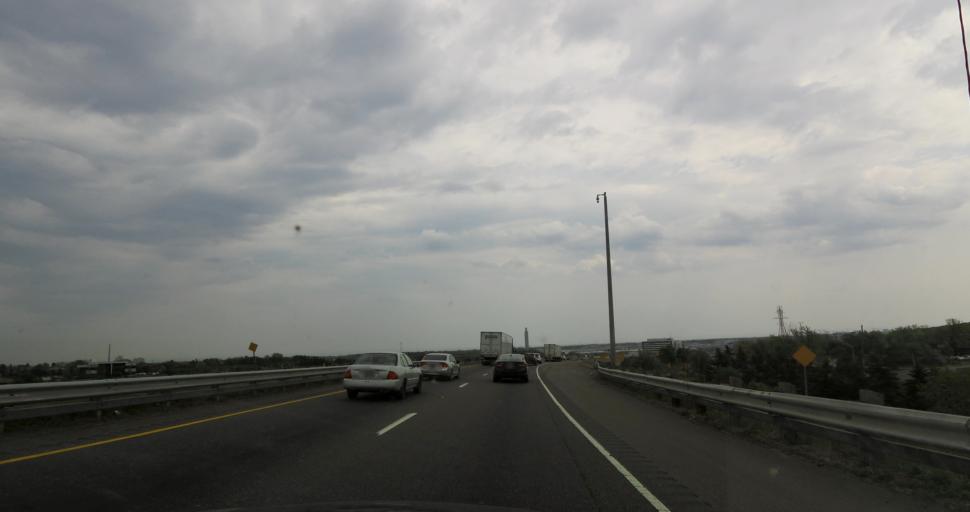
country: CA
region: Ontario
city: Oakville
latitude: 43.5004
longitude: -79.6758
